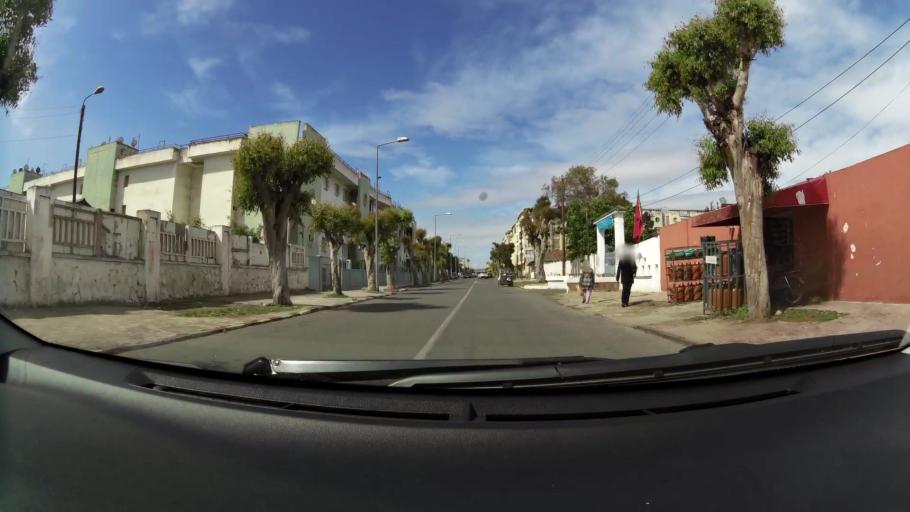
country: MA
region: Grand Casablanca
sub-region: Casablanca
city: Casablanca
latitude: 33.5853
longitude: -7.5881
